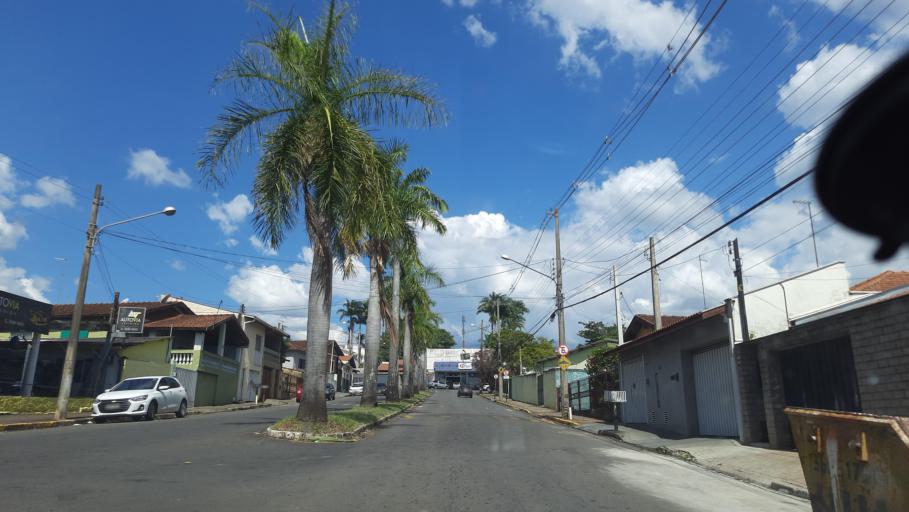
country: BR
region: Sao Paulo
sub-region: Sao Jose Do Rio Pardo
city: Sao Jose do Rio Pardo
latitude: -21.6035
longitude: -46.8990
